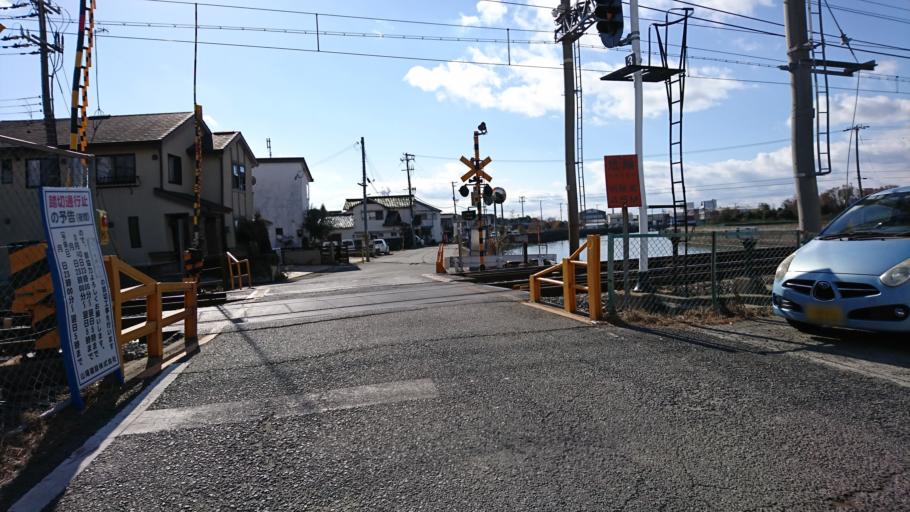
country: JP
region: Hyogo
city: Shirahamacho-usazakiminami
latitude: 34.7756
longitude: 134.7708
